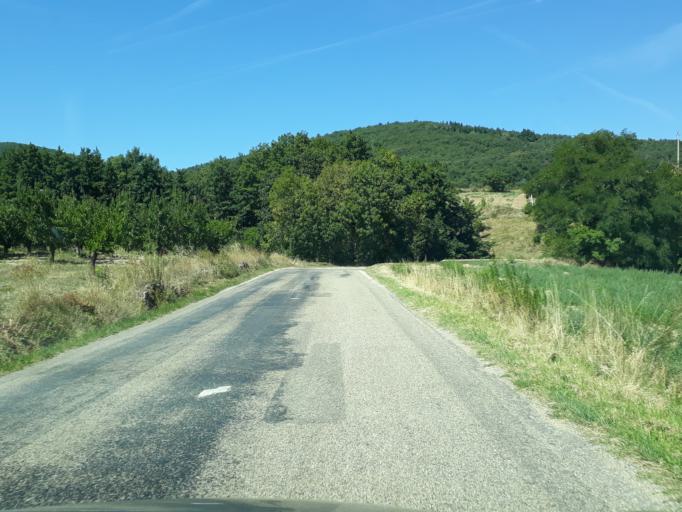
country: FR
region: Rhone-Alpes
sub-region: Departement de l'Ardeche
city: Felines
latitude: 45.3066
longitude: 4.7295
